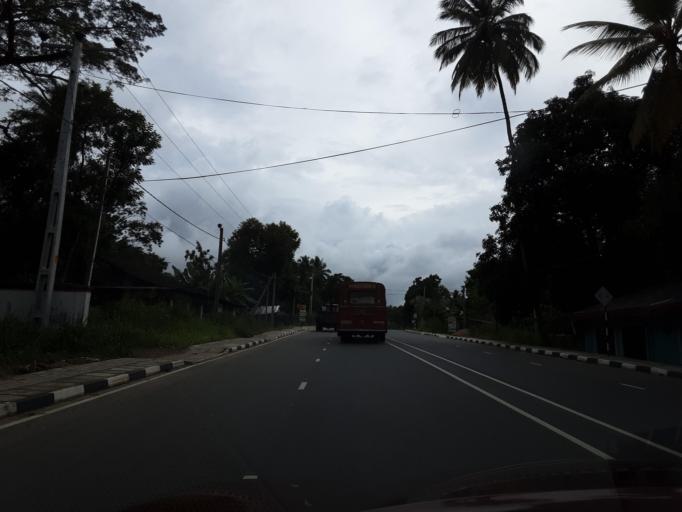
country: LK
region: Uva
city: Badulla
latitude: 7.3976
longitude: 81.2412
